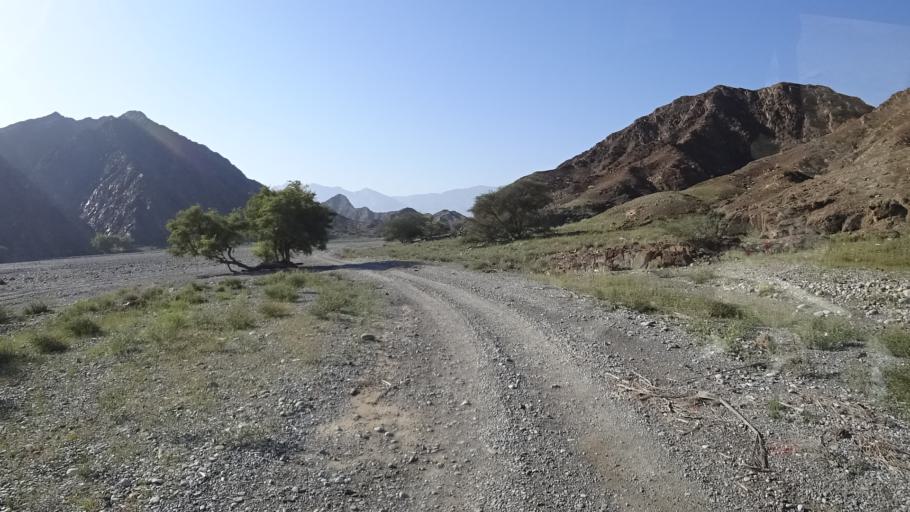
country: OM
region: Al Batinah
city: Bayt al `Awabi
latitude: 23.4031
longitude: 57.6658
